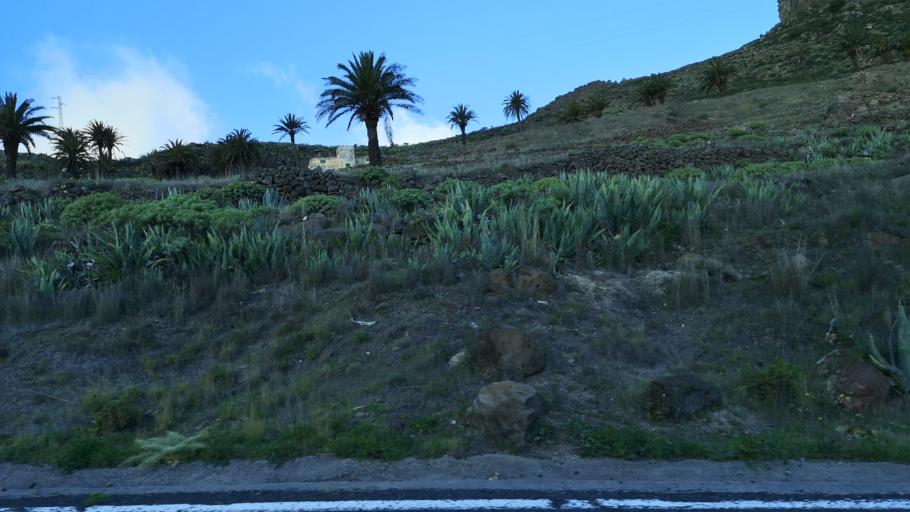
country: ES
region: Canary Islands
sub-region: Provincia de Santa Cruz de Tenerife
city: Alajero
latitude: 28.0756
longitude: -17.2395
